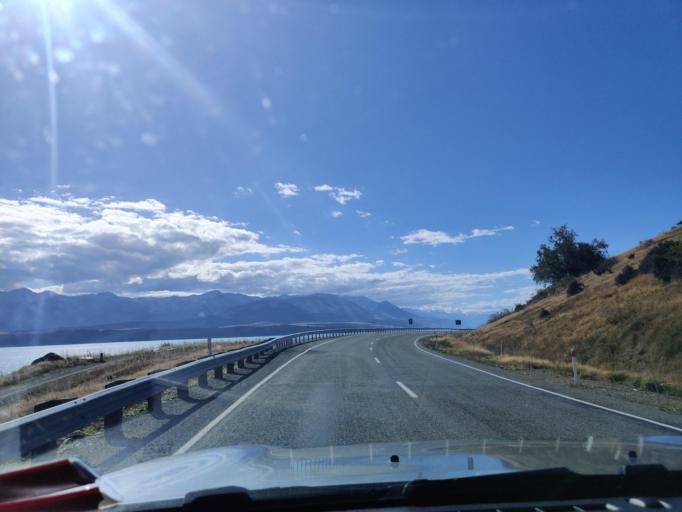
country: NZ
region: Canterbury
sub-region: Timaru District
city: Pleasant Point
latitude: -44.1789
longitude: 170.1562
